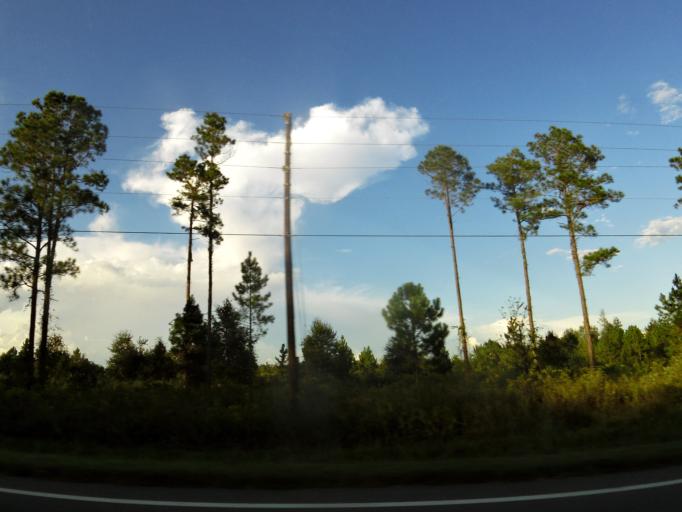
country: US
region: Georgia
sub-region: Lowndes County
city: Valdosta
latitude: 30.8052
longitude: -83.2064
